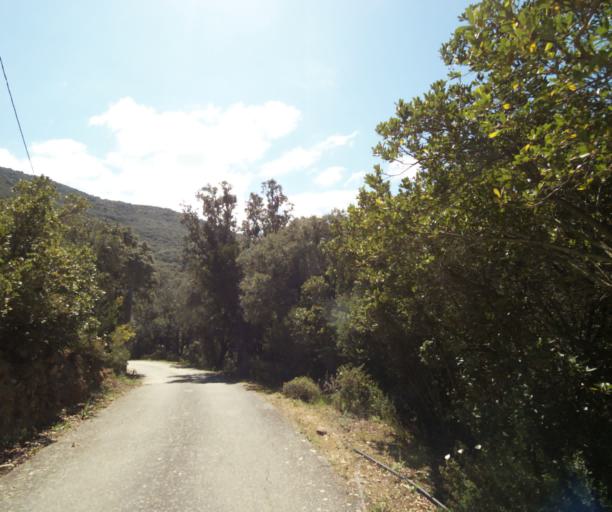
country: FR
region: Corsica
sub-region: Departement de la Corse-du-Sud
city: Propriano
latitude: 41.6397
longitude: 8.8688
